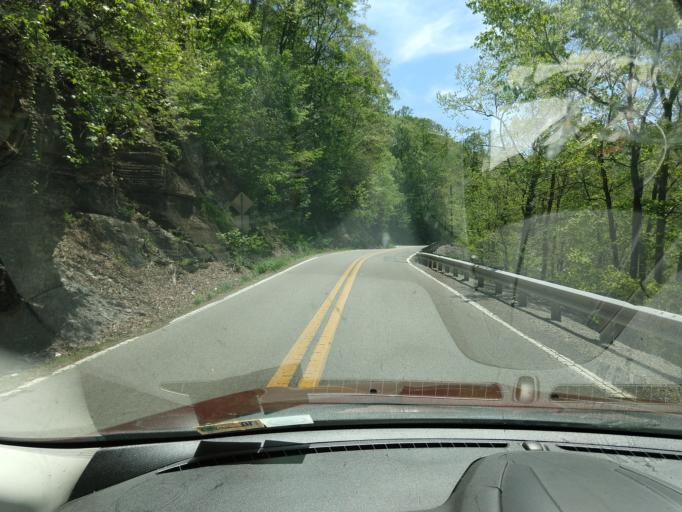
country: US
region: West Virginia
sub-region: McDowell County
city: Welch
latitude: 37.3195
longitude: -81.6949
